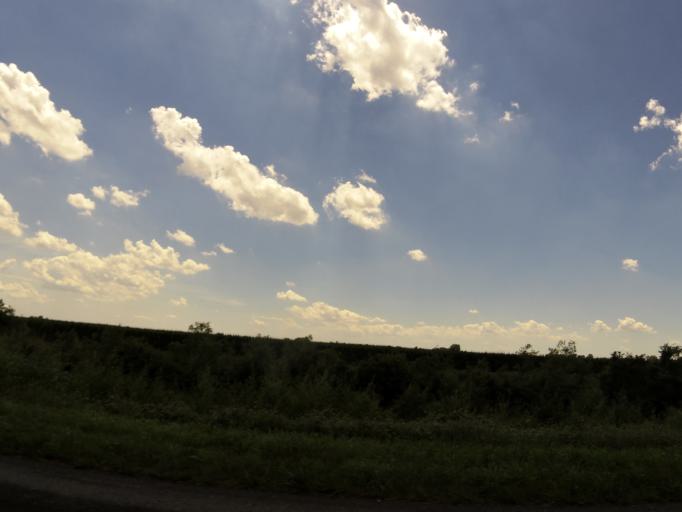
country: US
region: Missouri
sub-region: Pemiscot County
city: Caruthersville
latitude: 36.1619
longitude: -89.6793
